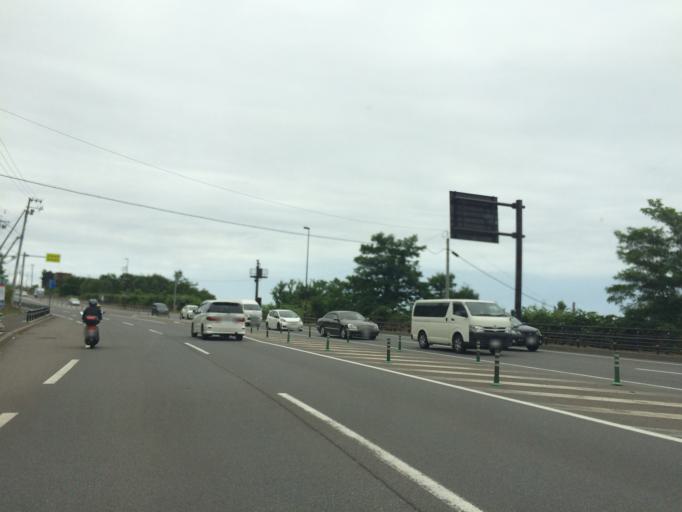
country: JP
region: Hokkaido
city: Otaru
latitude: 43.1509
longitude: 141.1322
